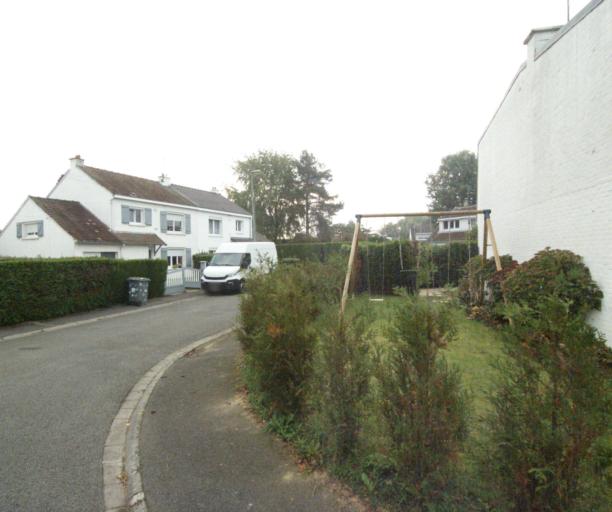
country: FR
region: Nord-Pas-de-Calais
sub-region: Departement du Nord
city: Seclin
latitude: 50.5424
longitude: 3.0189
